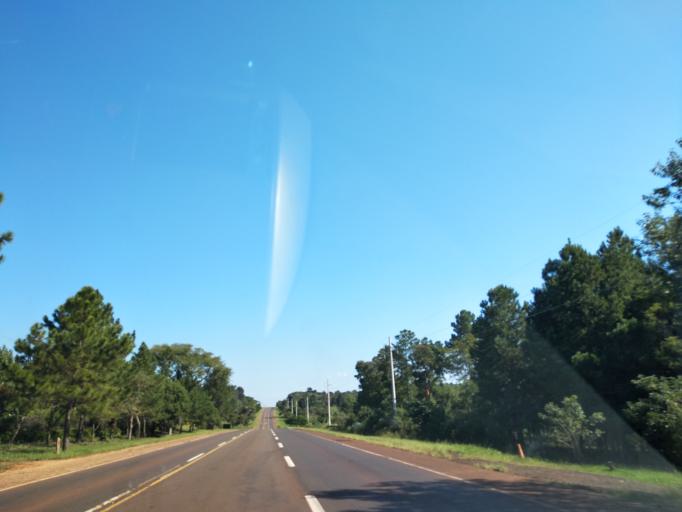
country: AR
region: Misiones
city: Capiovi
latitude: -26.8775
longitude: -55.0501
